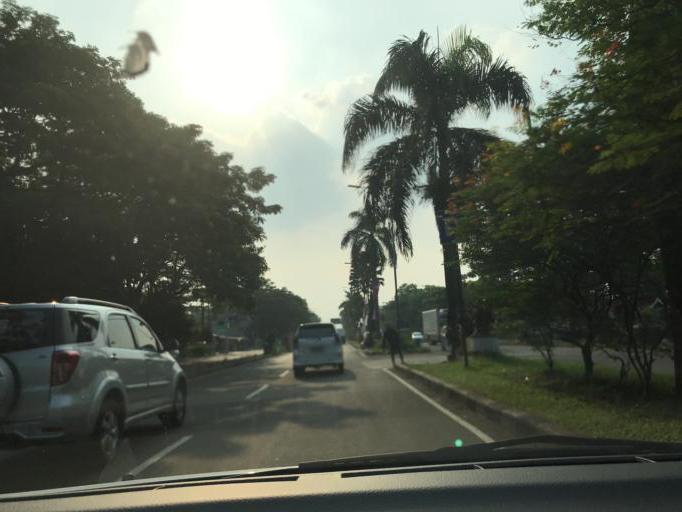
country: ID
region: West Java
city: Cibinong
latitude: -6.5205
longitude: 106.8386
